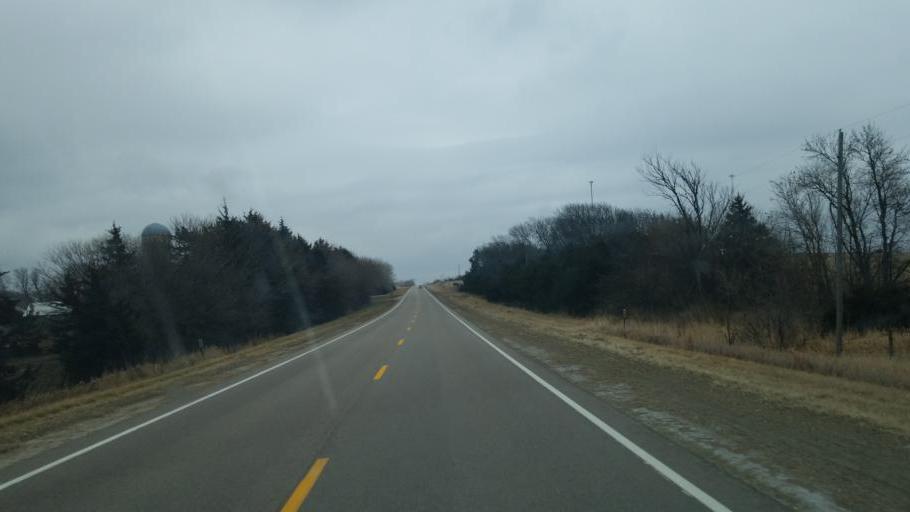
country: US
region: South Dakota
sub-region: Yankton County
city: Yankton
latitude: 42.7287
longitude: -97.4648
